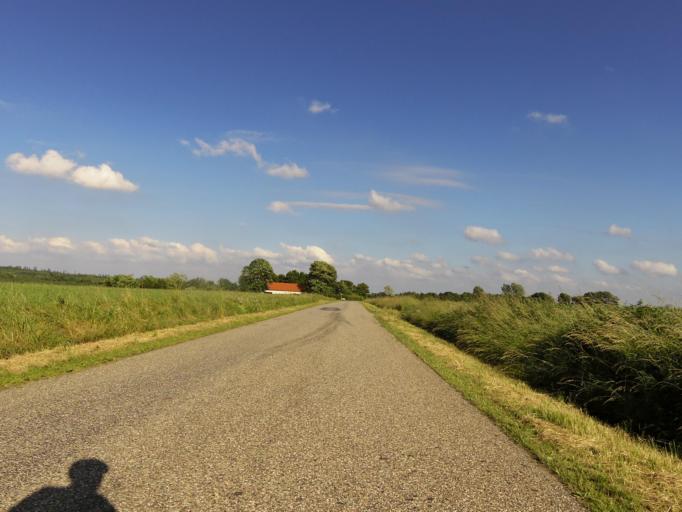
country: DK
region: South Denmark
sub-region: Vejen Kommune
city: Rodding
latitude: 55.3264
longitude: 9.1760
